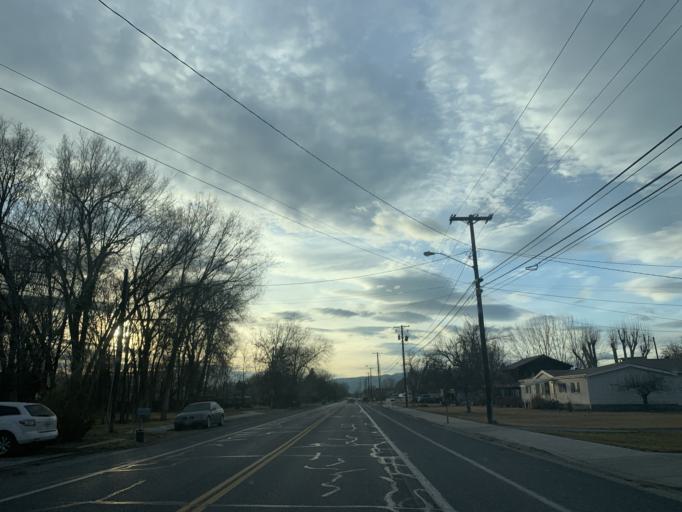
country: US
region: Utah
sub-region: Utah County
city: Provo
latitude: 40.2258
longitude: -111.6808
